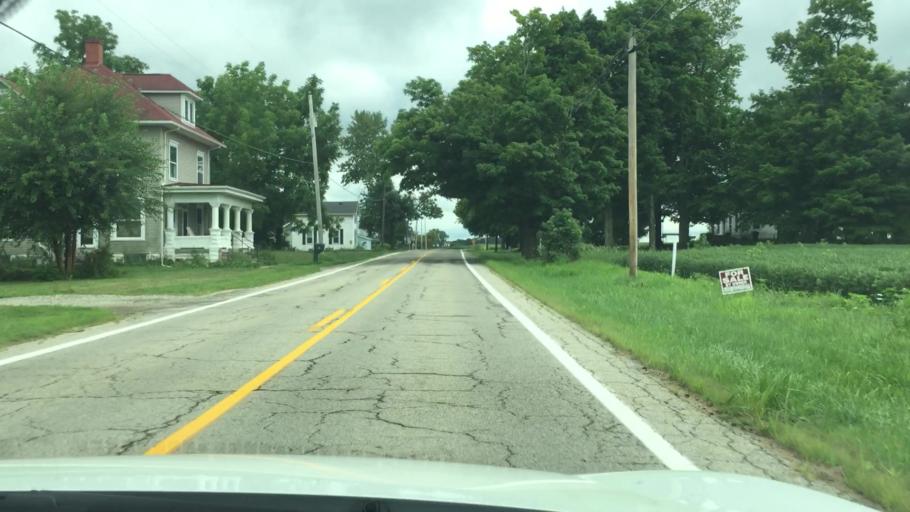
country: US
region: Ohio
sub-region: Champaign County
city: North Lewisburg
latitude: 40.1715
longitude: -83.5277
